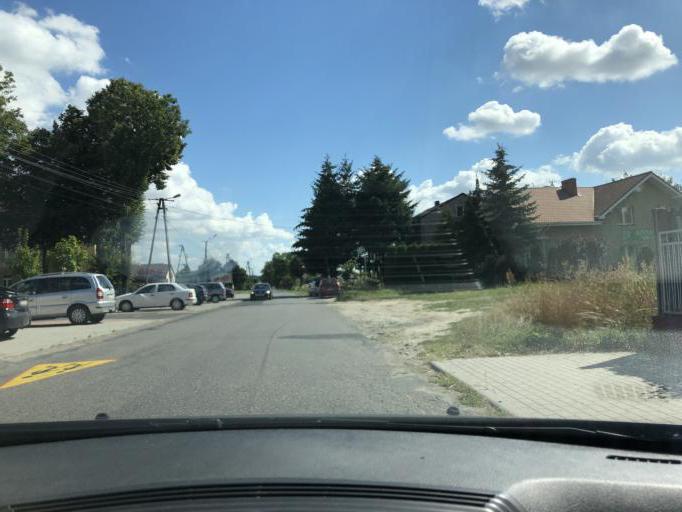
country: PL
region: Lodz Voivodeship
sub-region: Powiat wieruszowski
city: Czastary
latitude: 51.2585
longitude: 18.3226
